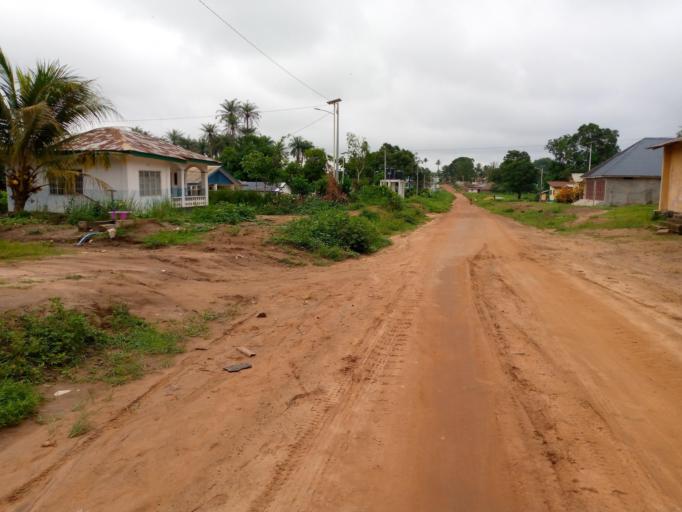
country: SL
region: Southern Province
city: Sumbuya
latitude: 7.5670
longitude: -12.0900
